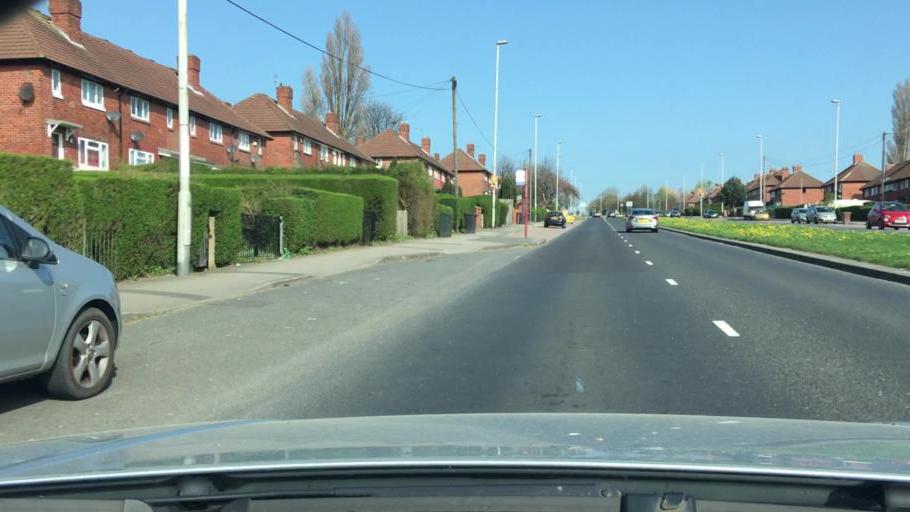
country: GB
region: England
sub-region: City and Borough of Leeds
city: Chapel Allerton
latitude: 53.8192
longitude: -1.5412
